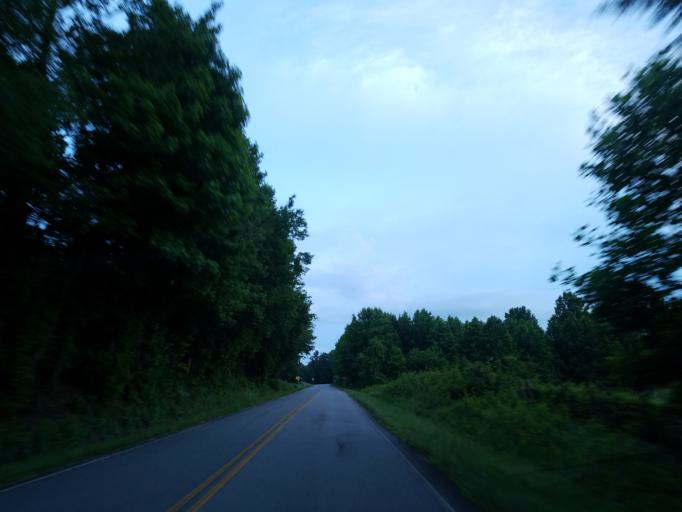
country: US
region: Georgia
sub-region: Dawson County
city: Dawsonville
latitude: 34.4687
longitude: -84.1782
